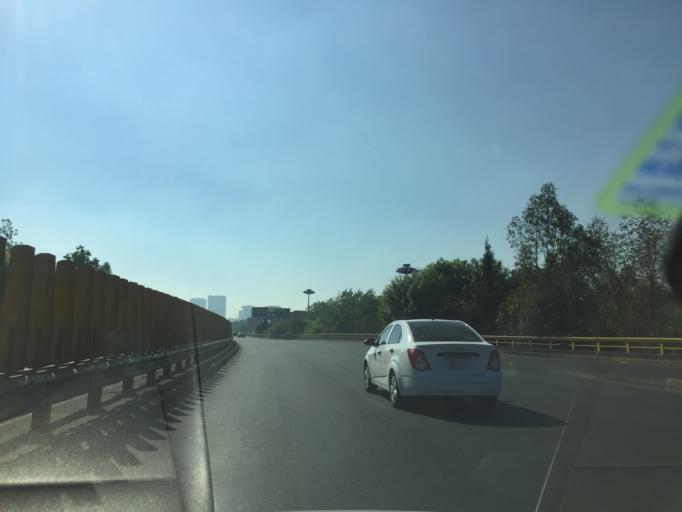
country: MX
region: Mexico City
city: Azcapotzalco
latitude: 19.4611
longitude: -99.1902
